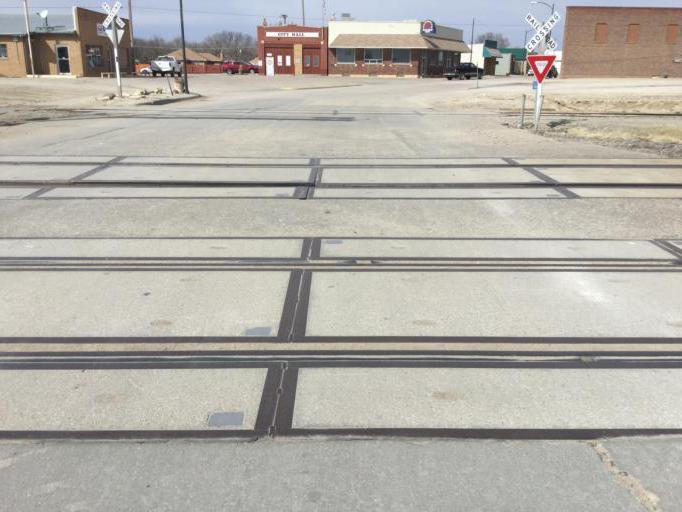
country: US
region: Kansas
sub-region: Ellis County
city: Victoria
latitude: 38.8498
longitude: -99.1459
